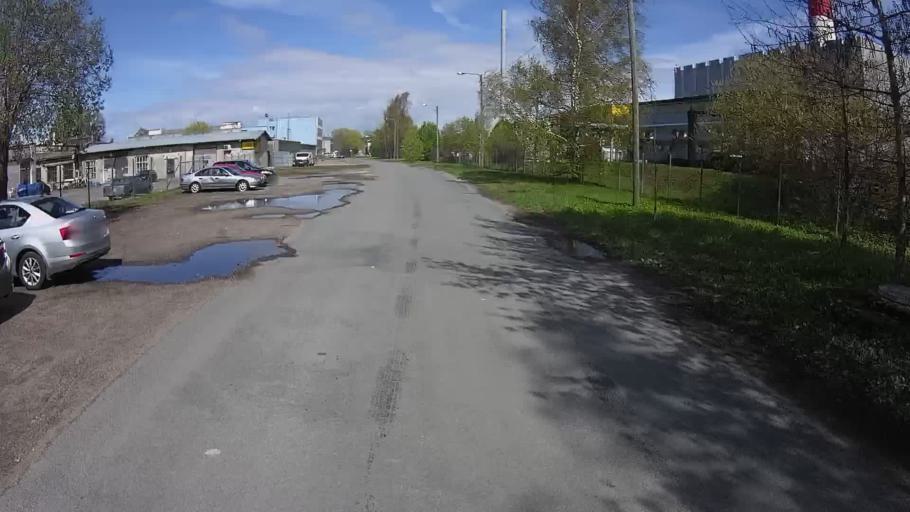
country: EE
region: Harju
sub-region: Tallinna linn
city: Tallinn
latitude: 59.4226
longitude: 24.6908
